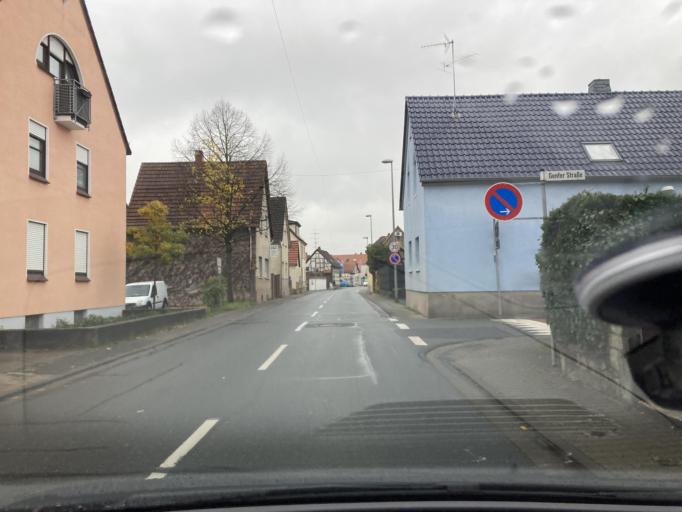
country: DE
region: Hesse
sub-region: Regierungsbezirk Darmstadt
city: Bischofsheim
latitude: 49.9612
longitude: 8.3815
